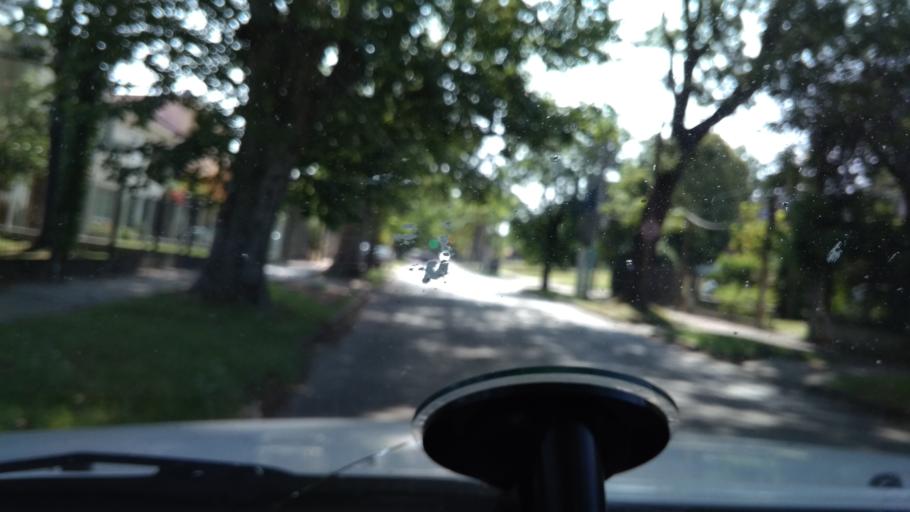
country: UY
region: Canelones
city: Paso de Carrasco
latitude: -34.8908
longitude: -56.0773
